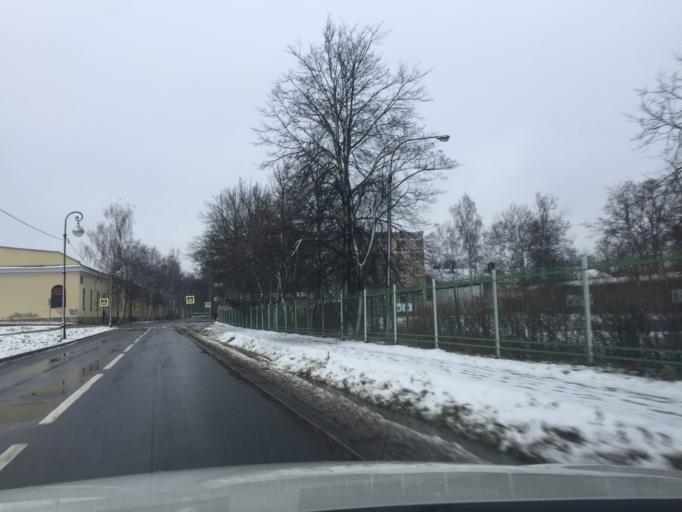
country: RU
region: St.-Petersburg
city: Pushkin
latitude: 59.7058
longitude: 30.3955
